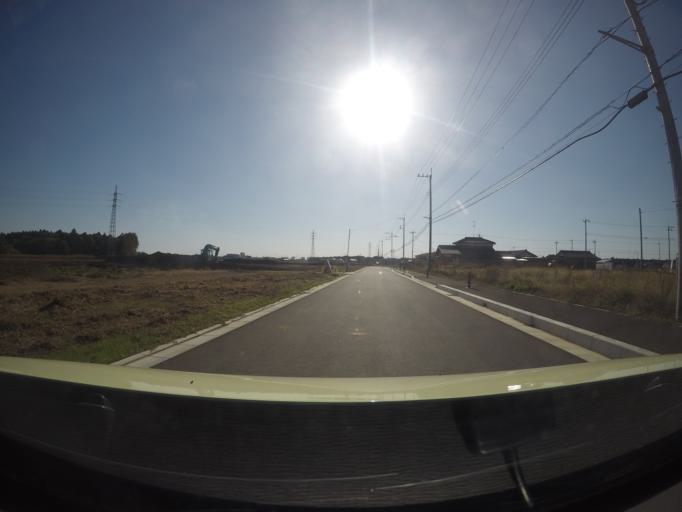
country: JP
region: Ibaraki
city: Naka
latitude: 36.1075
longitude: 140.1259
